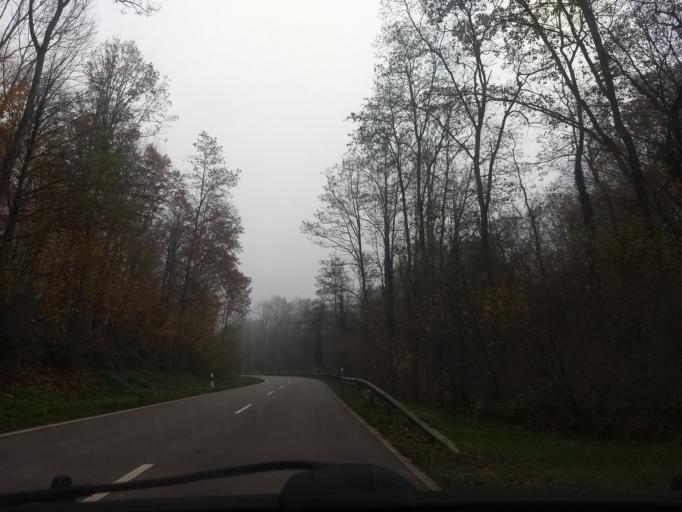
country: DE
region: Baden-Wuerttemberg
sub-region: Karlsruhe Region
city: Kuppenheim
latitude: 48.8125
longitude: 8.2418
